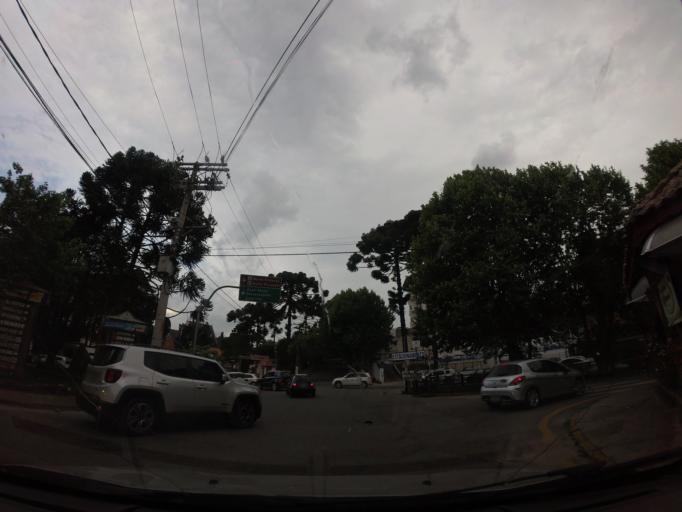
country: BR
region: Sao Paulo
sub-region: Campos Do Jordao
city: Campos do Jordao
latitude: -22.7178
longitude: -45.5649
